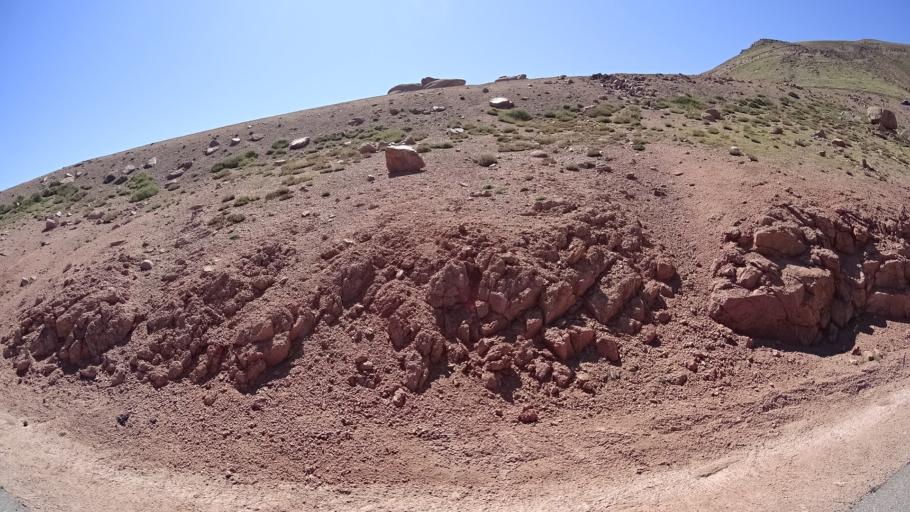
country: US
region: Colorado
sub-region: El Paso County
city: Cascade-Chipita Park
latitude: 38.8703
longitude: -105.0667
